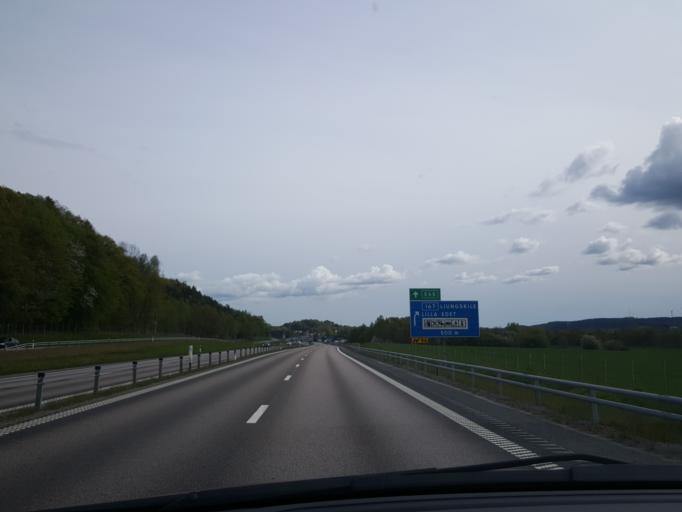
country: SE
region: Vaestra Goetaland
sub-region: Lilla Edets Kommun
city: Lilla Edet
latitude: 58.1564
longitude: 12.1356
